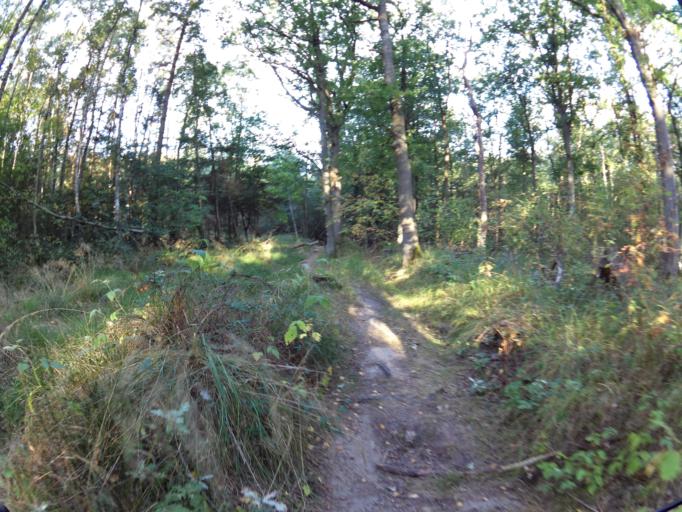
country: DE
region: North Rhine-Westphalia
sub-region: Regierungsbezirk Koln
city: Gangelt
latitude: 50.9672
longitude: 6.0136
